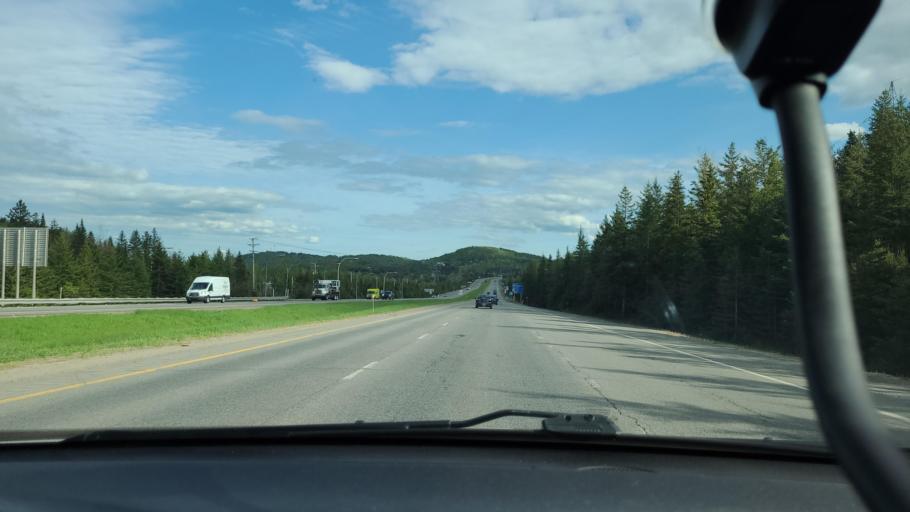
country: CA
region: Quebec
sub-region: Laurentides
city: Sainte-Agathe-des-Monts
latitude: 46.0581
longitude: -74.2746
